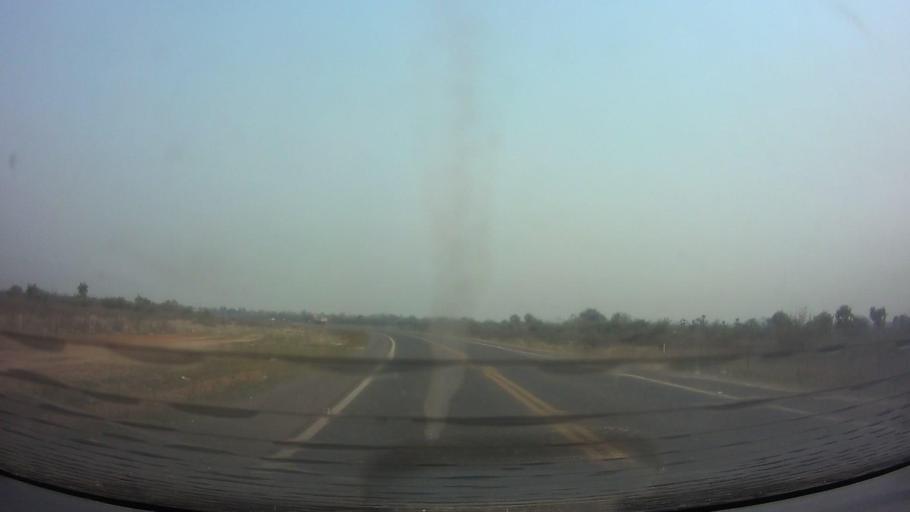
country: PY
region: Central
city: Limpio
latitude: -25.1599
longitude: -57.4905
